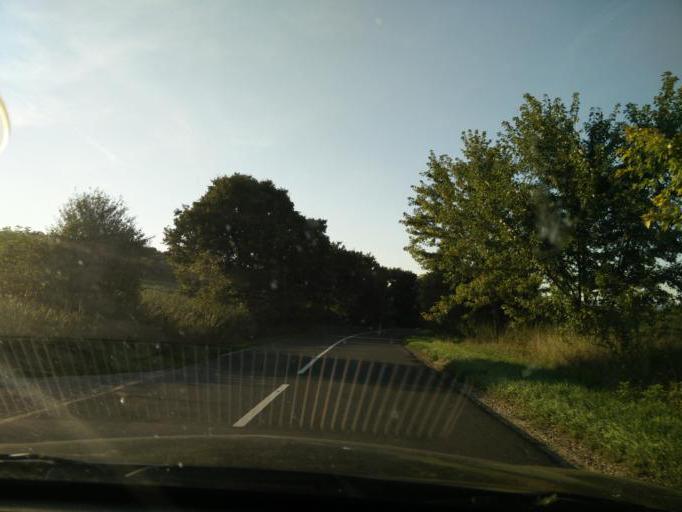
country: HU
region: Pest
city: Piliscsaba
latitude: 47.6423
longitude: 18.7835
